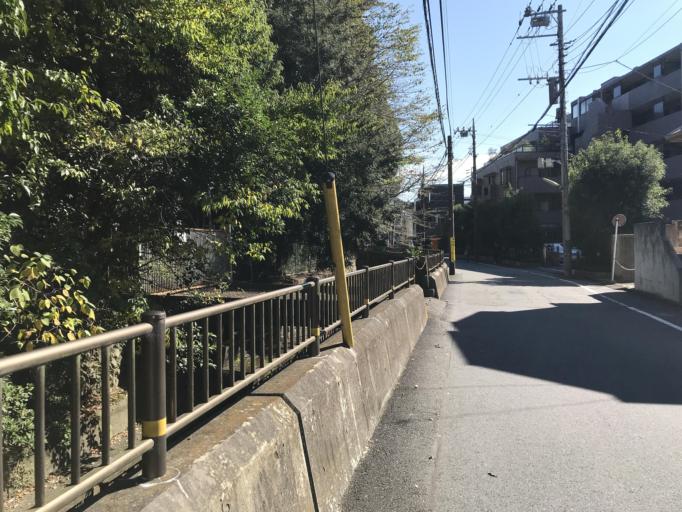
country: JP
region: Tokyo
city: Tokyo
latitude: 35.6061
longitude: 139.6372
